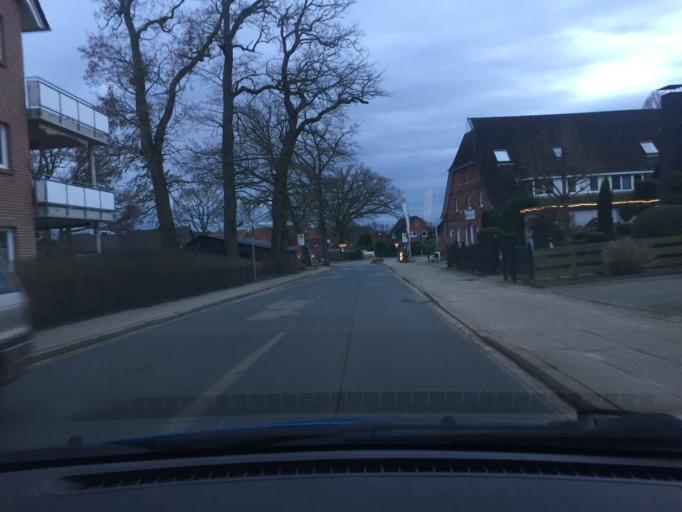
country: DE
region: Lower Saxony
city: Seevetal
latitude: 53.4340
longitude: 9.9063
